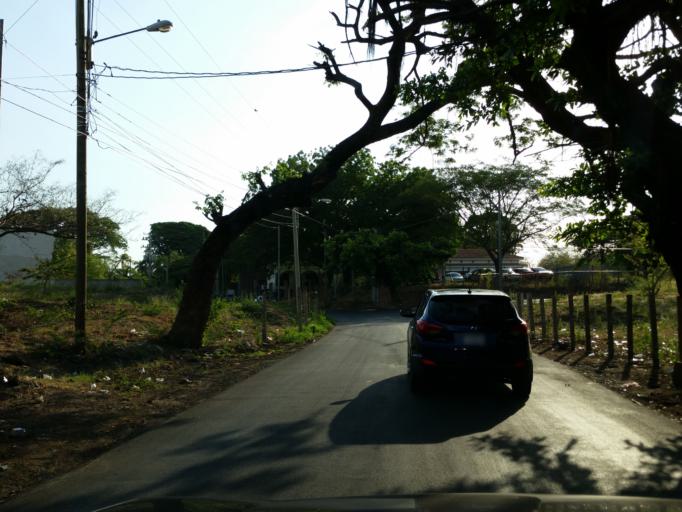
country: NI
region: Managua
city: Managua
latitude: 12.1234
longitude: -86.2676
